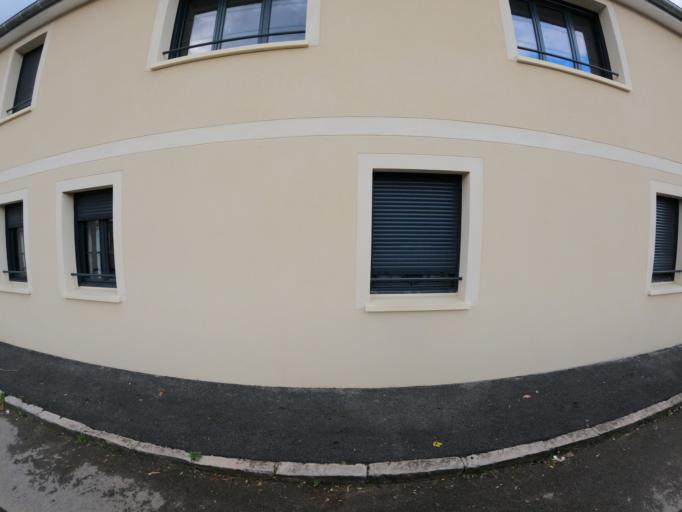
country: FR
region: Ile-de-France
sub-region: Departement de Seine-et-Marne
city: Coupvray
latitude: 48.8946
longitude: 2.7924
